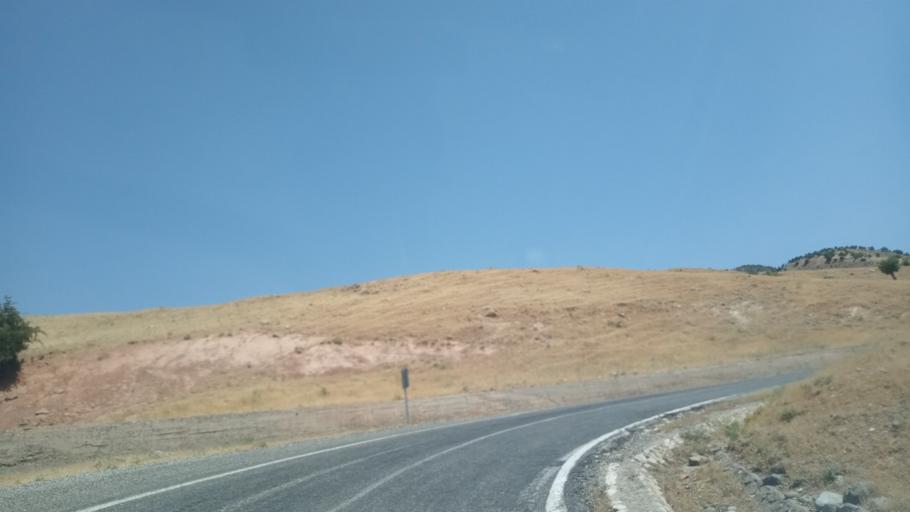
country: TR
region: Siirt
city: Dilektepe
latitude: 38.0626
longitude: 41.8312
